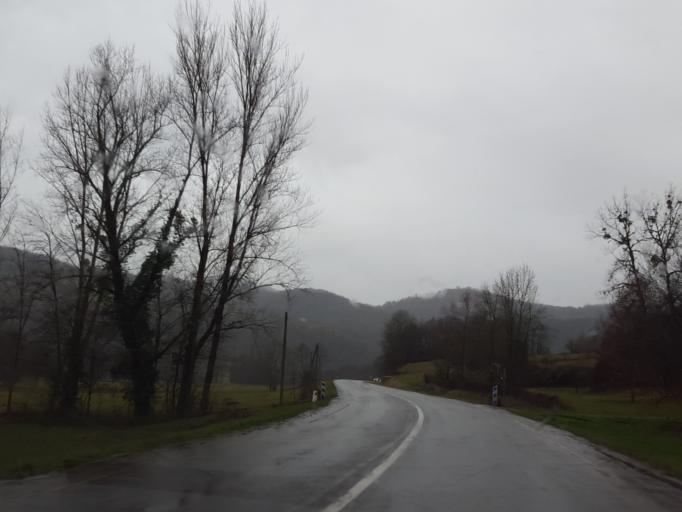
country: FR
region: Midi-Pyrenees
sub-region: Departement de l'Ariege
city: Montjoie-en-Couserans
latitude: 43.0145
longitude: 1.3686
